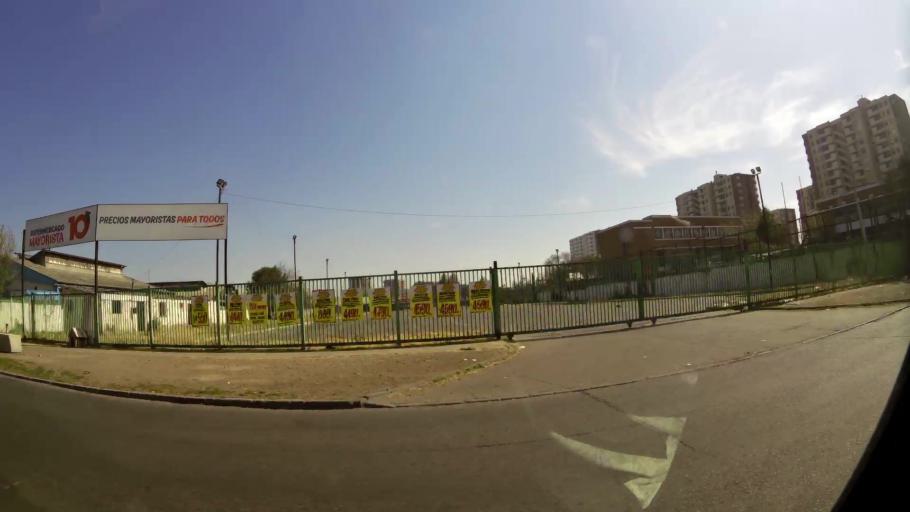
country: CL
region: Santiago Metropolitan
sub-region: Provincia de Santiago
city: Lo Prado
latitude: -33.4682
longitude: -70.7227
